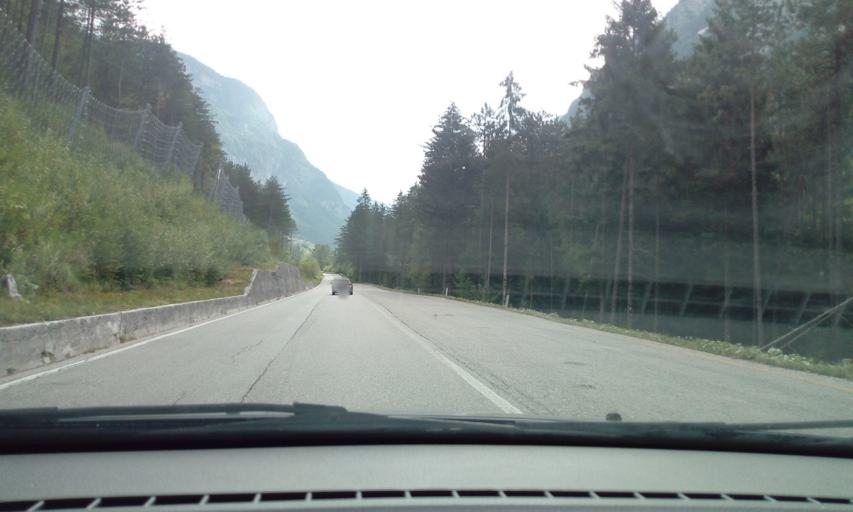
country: IT
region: Friuli Venezia Giulia
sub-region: Provincia di Udine
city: Chiusaforte
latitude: 46.4025
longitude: 13.4040
